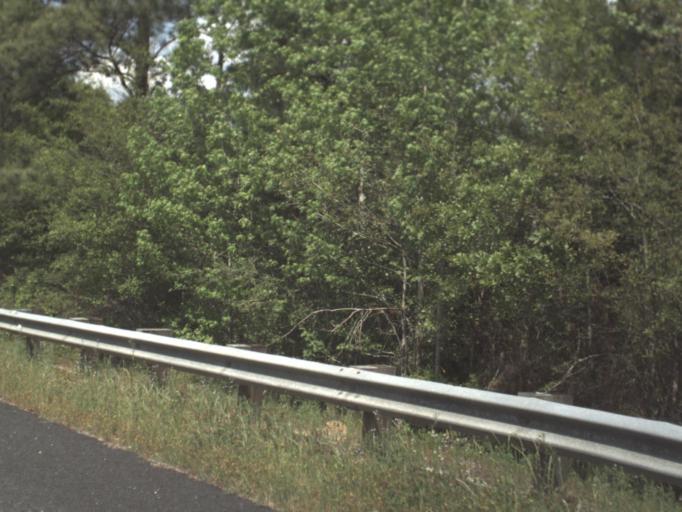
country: US
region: Florida
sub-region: Escambia County
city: Molino
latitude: 30.8496
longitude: -87.3218
